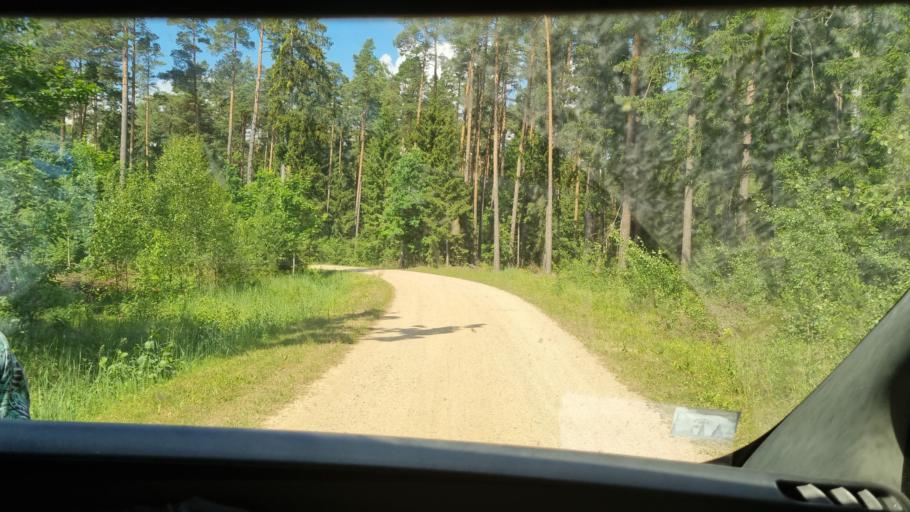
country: LV
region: Kuldigas Rajons
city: Kuldiga
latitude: 57.0610
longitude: 21.8167
